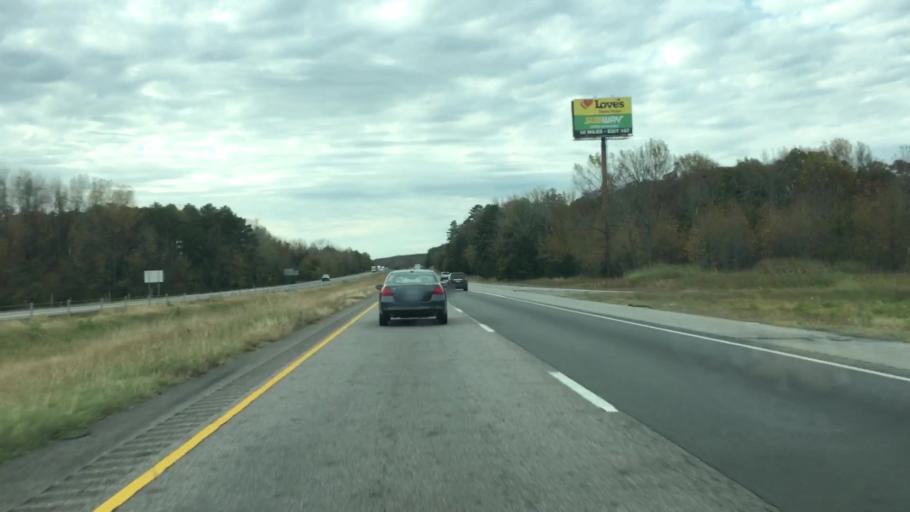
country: US
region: Arkansas
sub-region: Faulkner County
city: Conway
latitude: 35.1540
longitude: -92.5557
